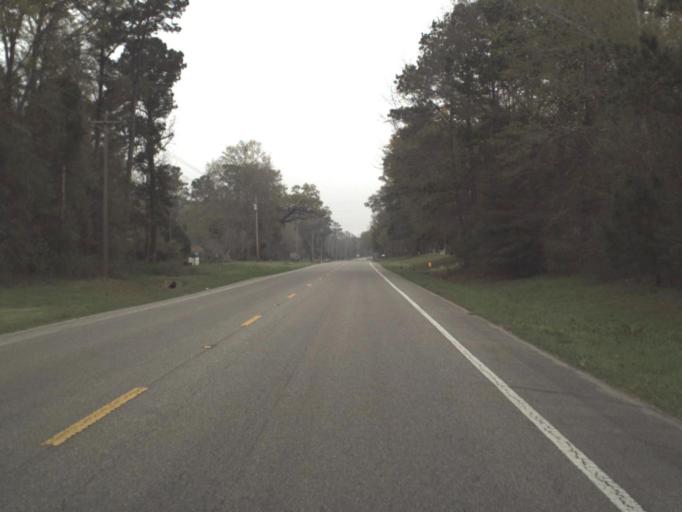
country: US
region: Florida
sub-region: Gadsden County
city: Gretna
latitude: 30.5801
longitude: -84.6727
